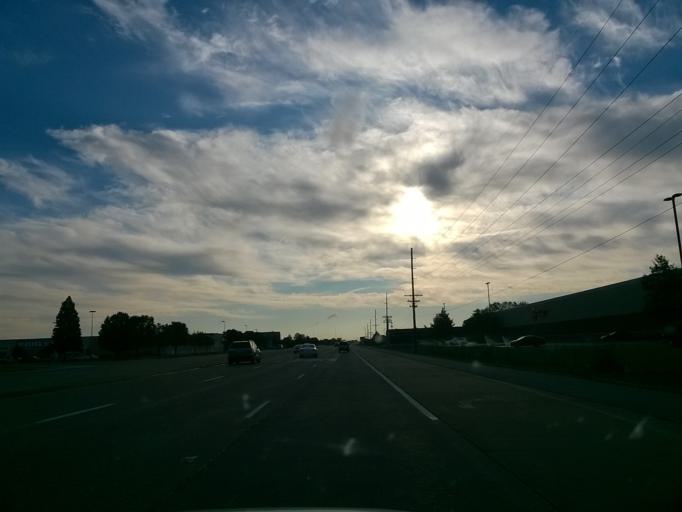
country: US
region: Indiana
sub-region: Vanderburgh County
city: Melody Hill
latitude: 37.9766
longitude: -87.4704
